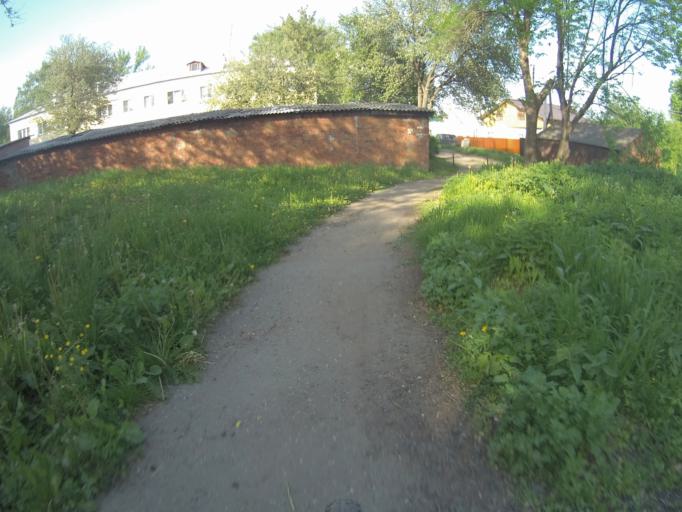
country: RU
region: Vladimir
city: Bogolyubovo
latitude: 56.1680
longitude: 40.4882
